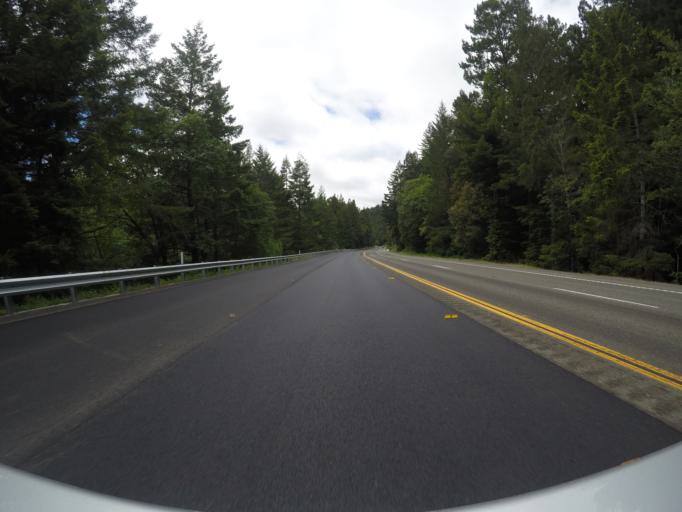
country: US
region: California
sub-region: Humboldt County
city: Redway
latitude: 40.3082
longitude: -123.9048
